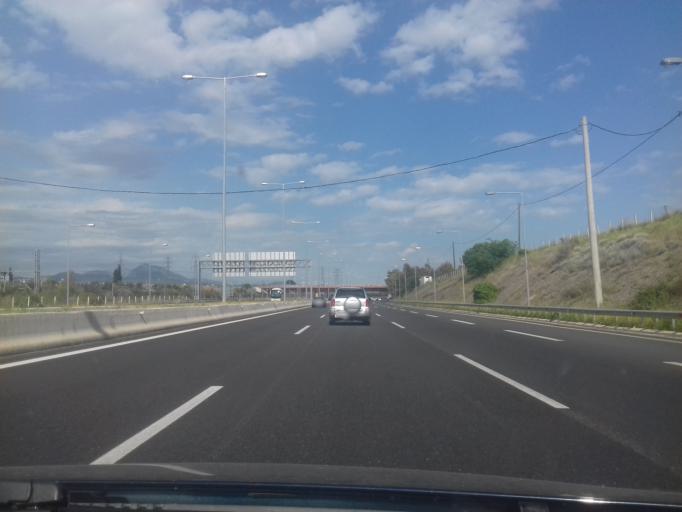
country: GR
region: Peloponnese
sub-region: Nomos Korinthias
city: Korinthos
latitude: 37.9215
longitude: 22.9407
